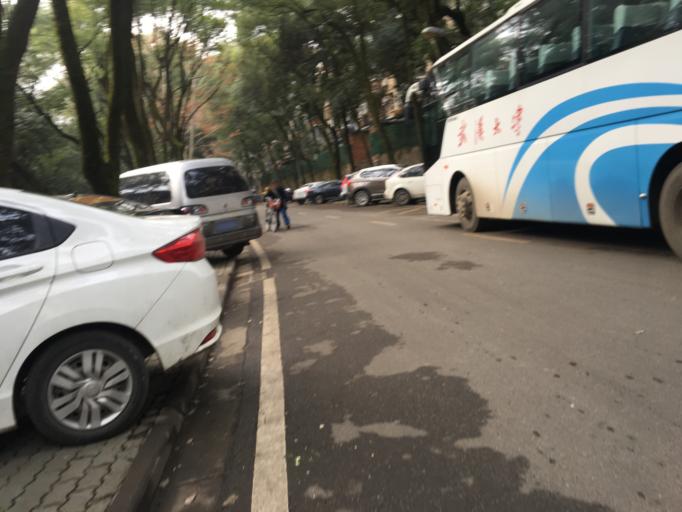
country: CN
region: Hubei
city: Guanshan
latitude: 30.5348
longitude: 114.3660
